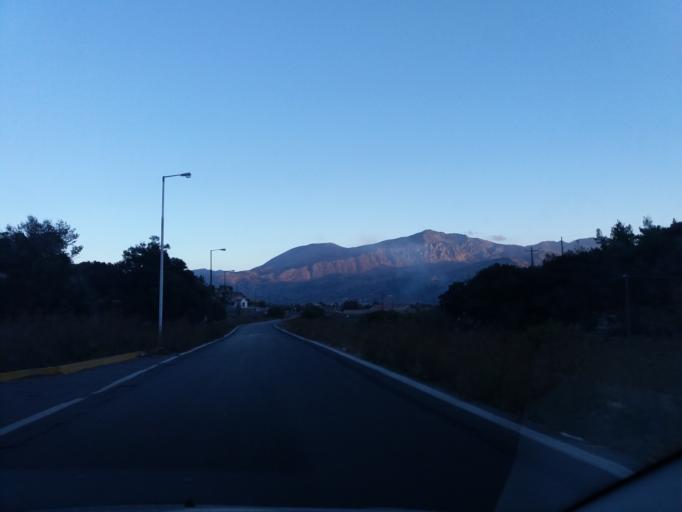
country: GR
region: Crete
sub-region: Nomos Irakleiou
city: Mokhos
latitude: 35.1993
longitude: 25.4608
